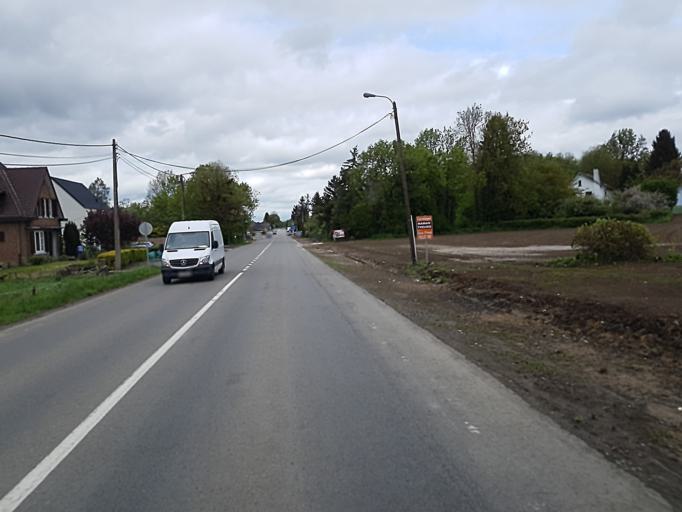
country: BE
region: Wallonia
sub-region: Province du Brabant Wallon
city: Jodoigne
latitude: 50.7401
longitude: 4.8803
